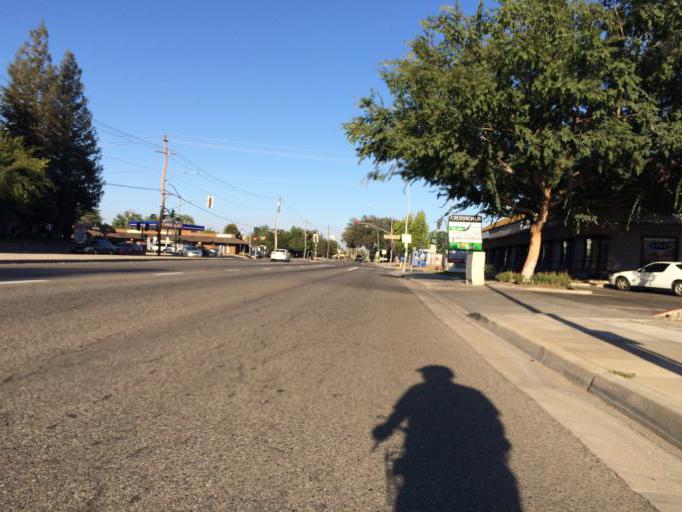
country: US
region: California
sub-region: Fresno County
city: Clovis
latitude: 36.8229
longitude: -119.7098
